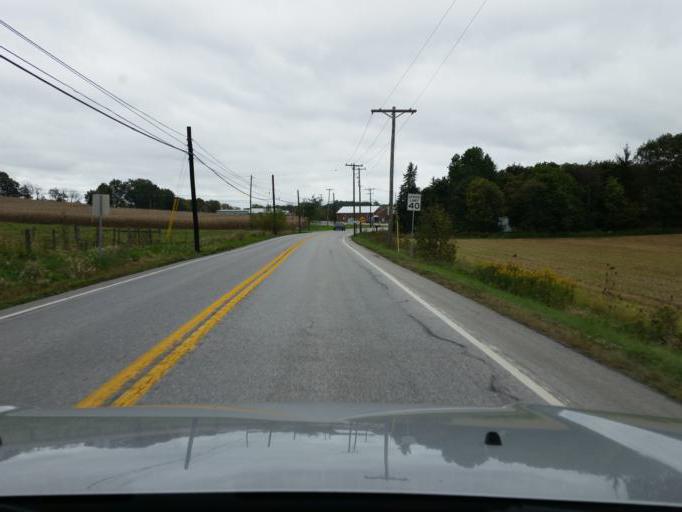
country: US
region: Pennsylvania
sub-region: Adams County
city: Biglerville
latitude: 39.9494
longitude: -77.1531
